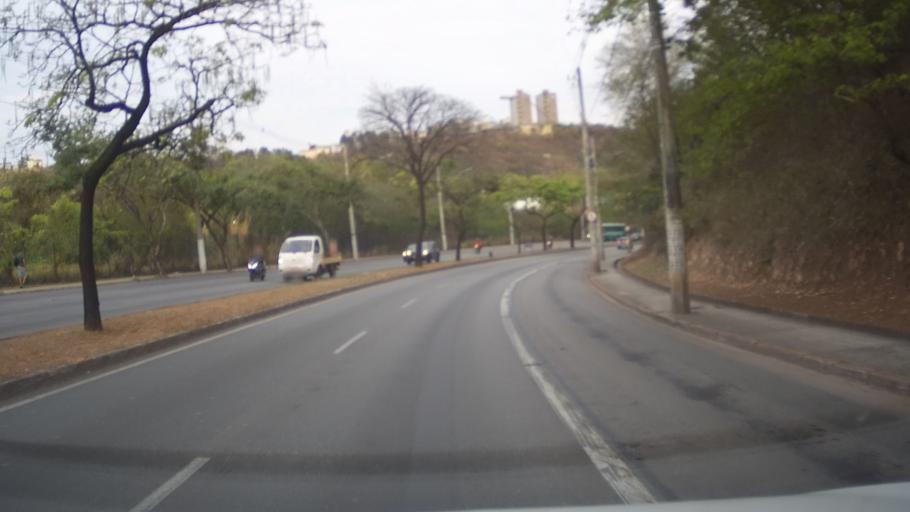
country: BR
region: Minas Gerais
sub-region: Belo Horizonte
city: Belo Horizonte
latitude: -19.8840
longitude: -43.9743
